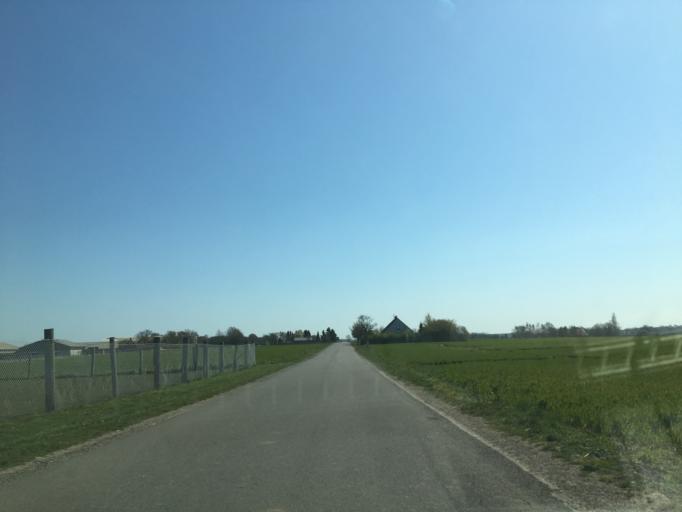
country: DK
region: Zealand
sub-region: Guldborgsund Kommune
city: Nykobing Falster
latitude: 54.7400
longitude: 11.7901
